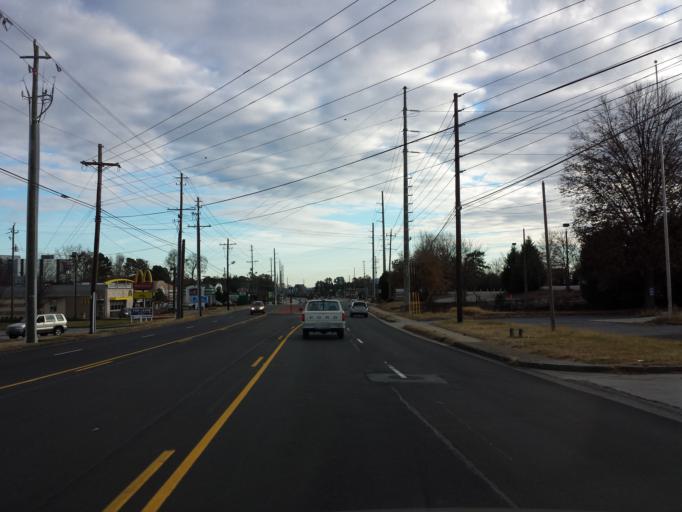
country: US
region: Georgia
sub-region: Cobb County
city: Vinings
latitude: 33.9210
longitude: -84.4676
